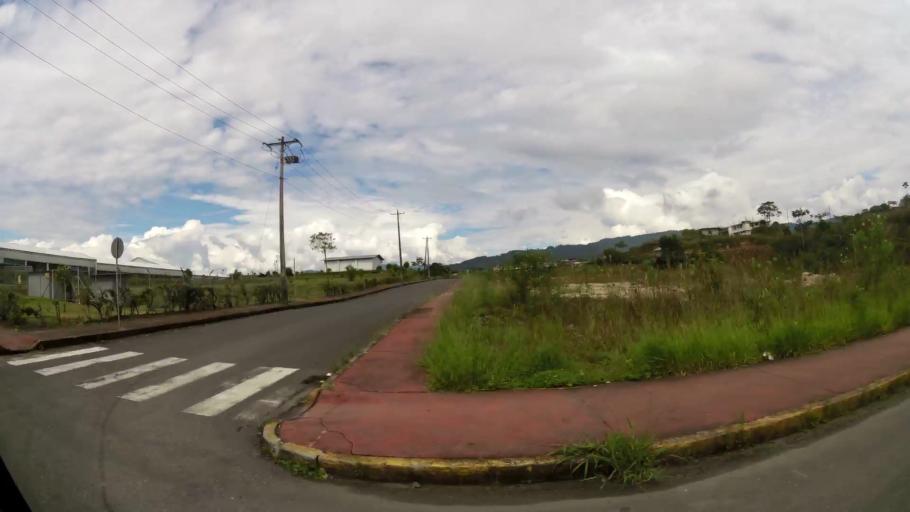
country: EC
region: Pastaza
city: Puyo
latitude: -1.5005
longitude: -78.0017
